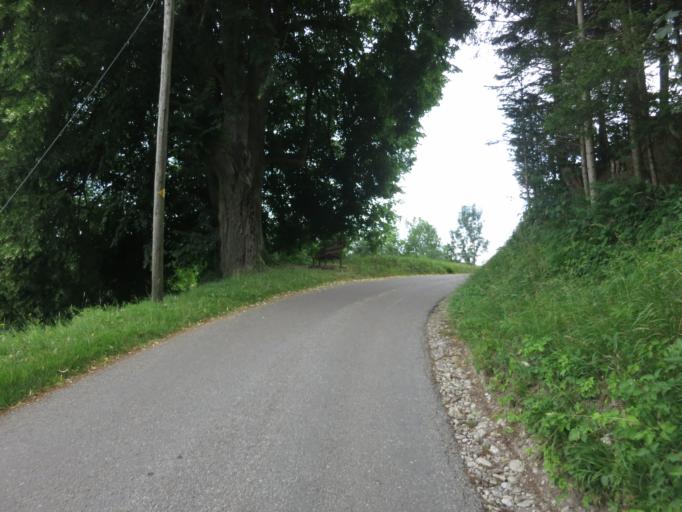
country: CH
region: Saint Gallen
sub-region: Wahlkreis Toggenburg
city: Ganterschwil
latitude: 47.3720
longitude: 9.0838
